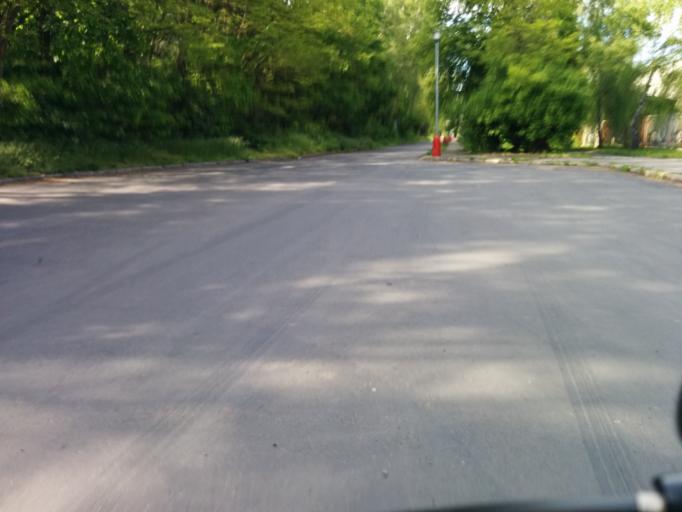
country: CZ
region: Central Bohemia
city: Neratovice
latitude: 50.2704
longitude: 14.5139
